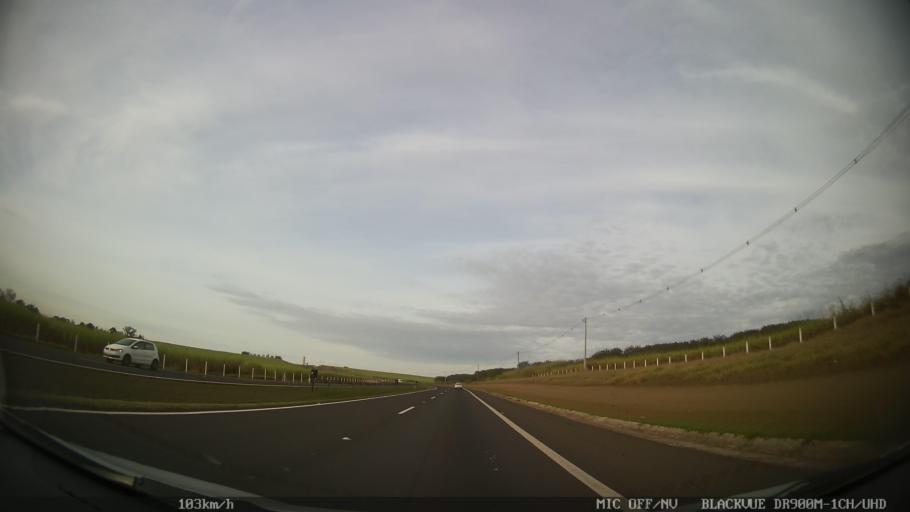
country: BR
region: Sao Paulo
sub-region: Piracicaba
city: Piracicaba
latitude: -22.6822
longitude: -47.5716
